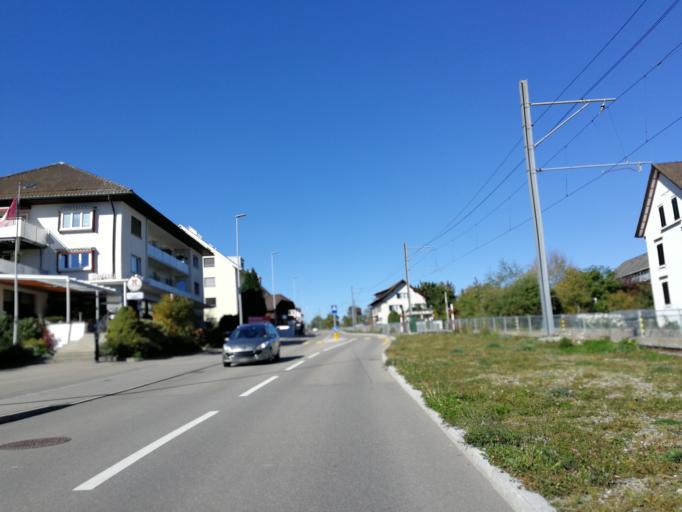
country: CH
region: Zurich
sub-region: Bezirk Uster
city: Hinteregg
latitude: 47.3069
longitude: 8.6829
